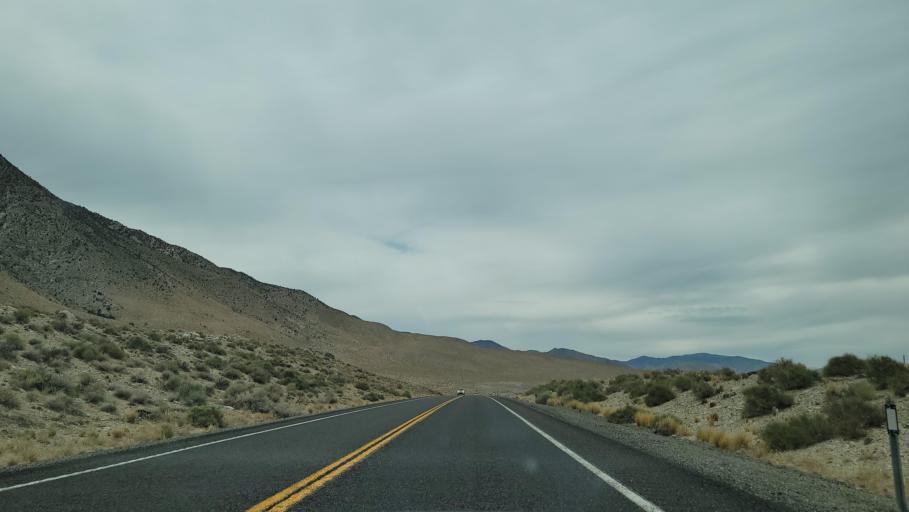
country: US
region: Nevada
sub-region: Mineral County
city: Hawthorne
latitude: 38.5790
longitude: -118.7020
